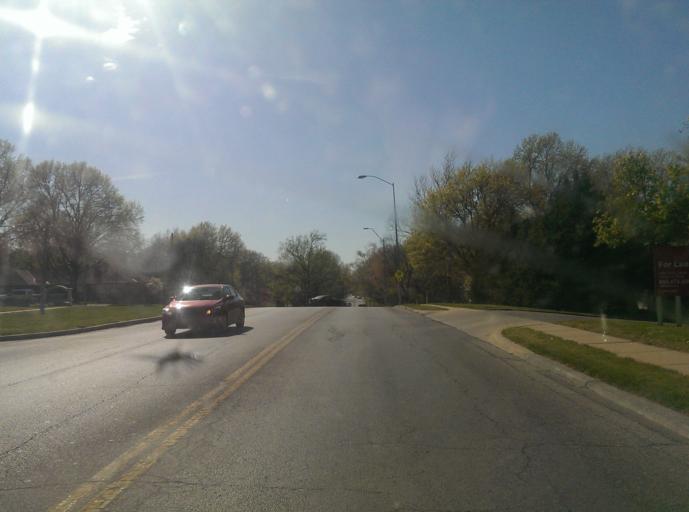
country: US
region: Kansas
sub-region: Johnson County
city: Leawood
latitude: 38.9261
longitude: -94.5872
